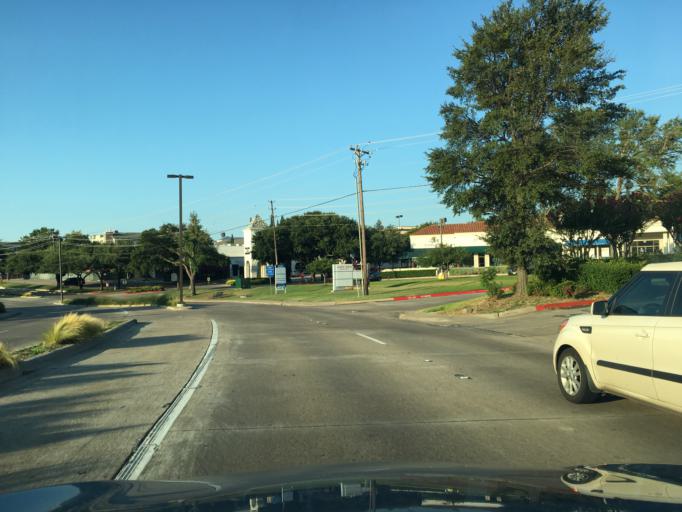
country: US
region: Texas
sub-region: Dallas County
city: Addison
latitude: 32.9526
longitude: -96.8187
